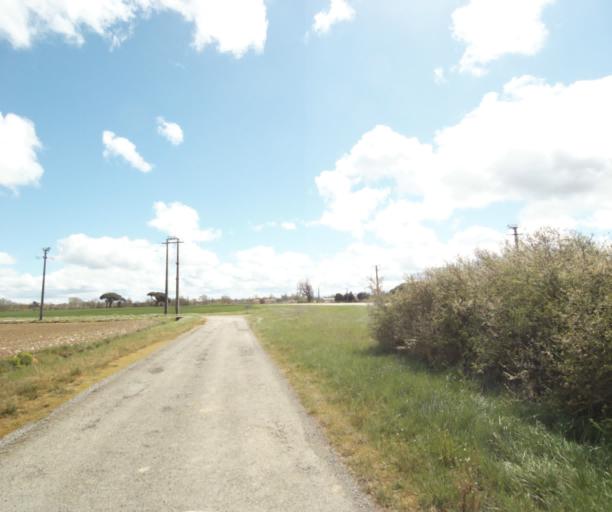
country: FR
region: Midi-Pyrenees
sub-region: Departement de l'Ariege
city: Saverdun
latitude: 43.2469
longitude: 1.5725
